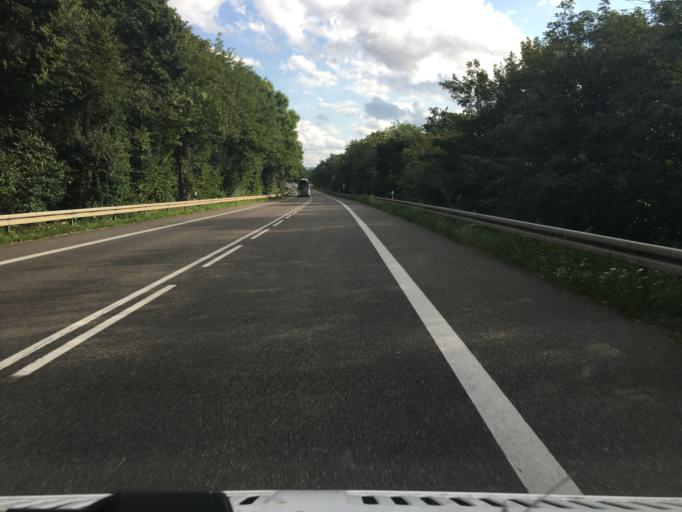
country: DE
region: North Rhine-Westphalia
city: Zulpich
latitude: 50.7114
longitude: 6.6484
